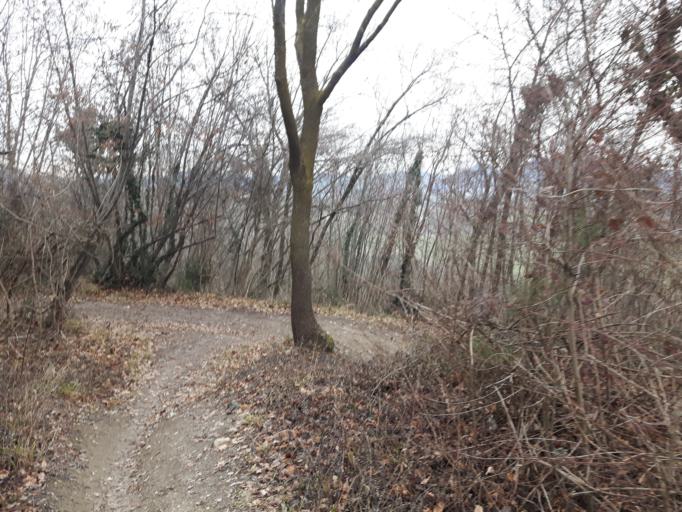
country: IT
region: Veneto
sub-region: Provincia di Padova
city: Arqua Petrarca
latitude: 45.2762
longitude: 11.7424
